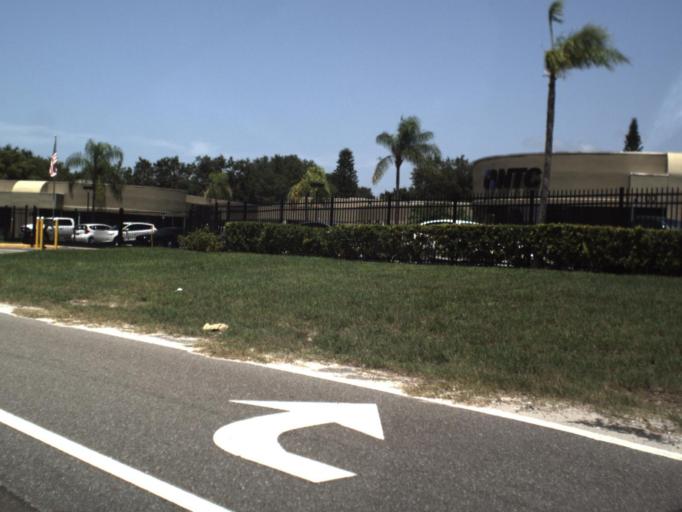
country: US
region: Florida
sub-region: Pinellas County
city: Palm Harbor
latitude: 28.0869
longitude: -82.7686
